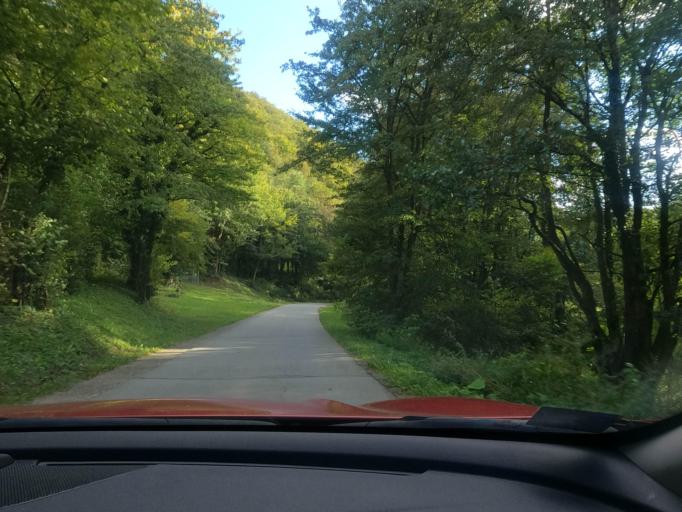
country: HR
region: Sisacko-Moslavacka
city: Petrinja
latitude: 45.3961
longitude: 16.2442
